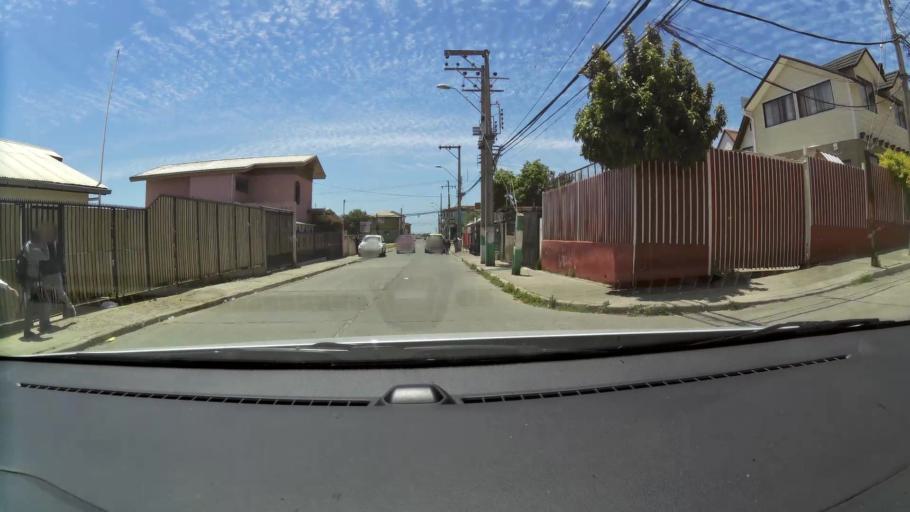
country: CL
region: Valparaiso
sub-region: Provincia de Valparaiso
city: Vina del Mar
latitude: -33.0477
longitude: -71.5824
